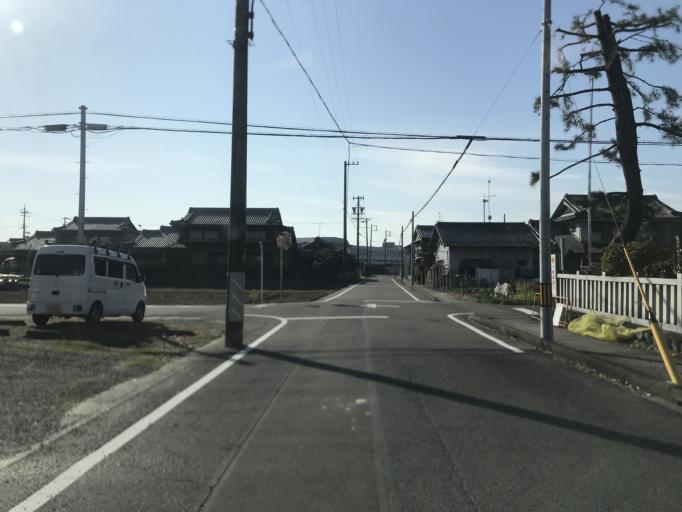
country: JP
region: Aichi
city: Iwakura
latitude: 35.2198
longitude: 136.8476
